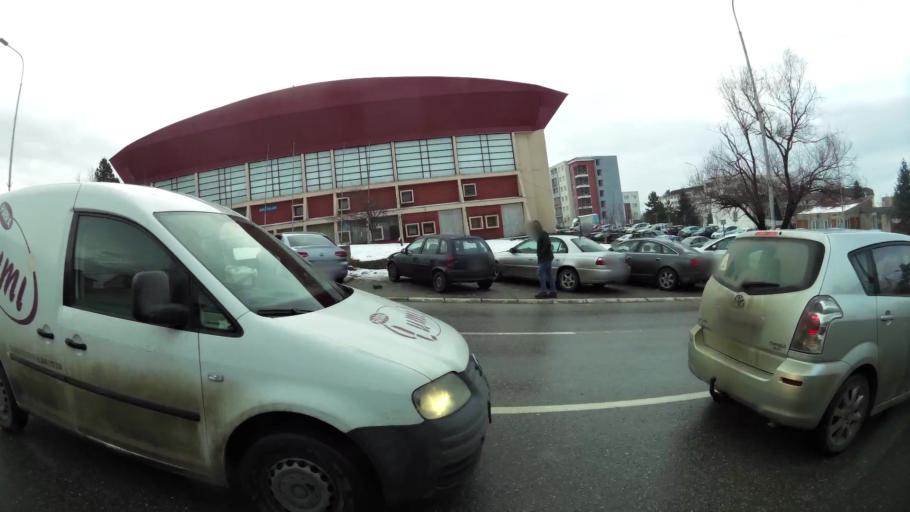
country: XK
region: Pristina
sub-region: Komuna e Prishtines
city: Pristina
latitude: 42.6545
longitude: 21.1661
